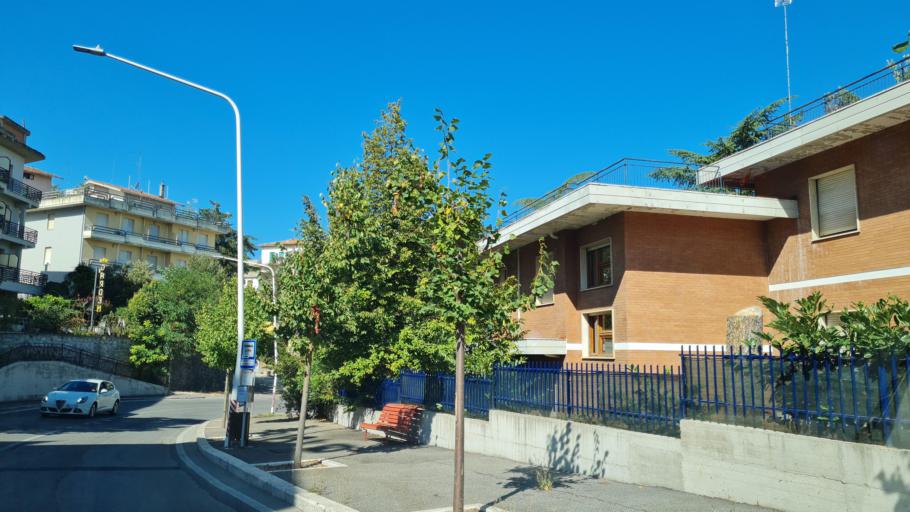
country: IT
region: Tuscany
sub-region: Provincia di Siena
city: Chianciano Terme
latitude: 43.0399
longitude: 11.8127
